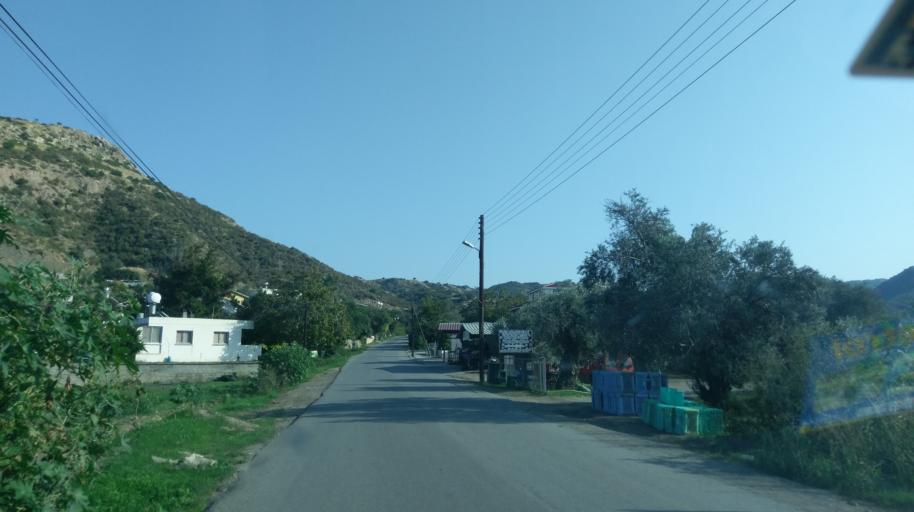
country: CY
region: Lefkosia
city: Kato Pyrgos
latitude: 35.1674
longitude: 32.7452
